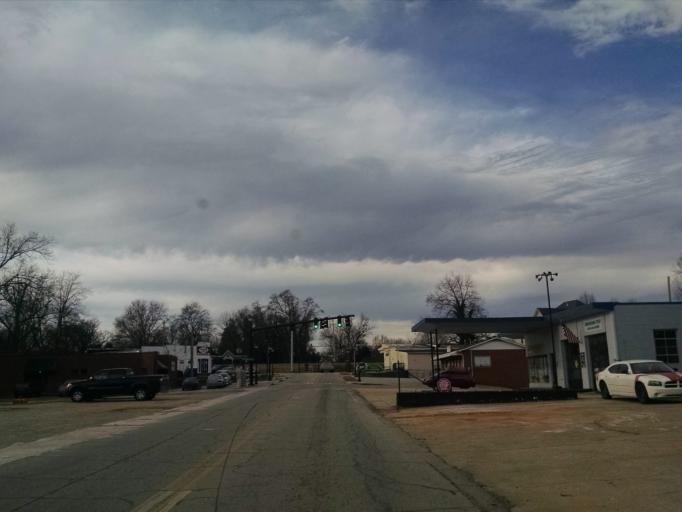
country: US
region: Georgia
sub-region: Gwinnett County
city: Buford
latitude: 34.1163
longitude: -84.0089
